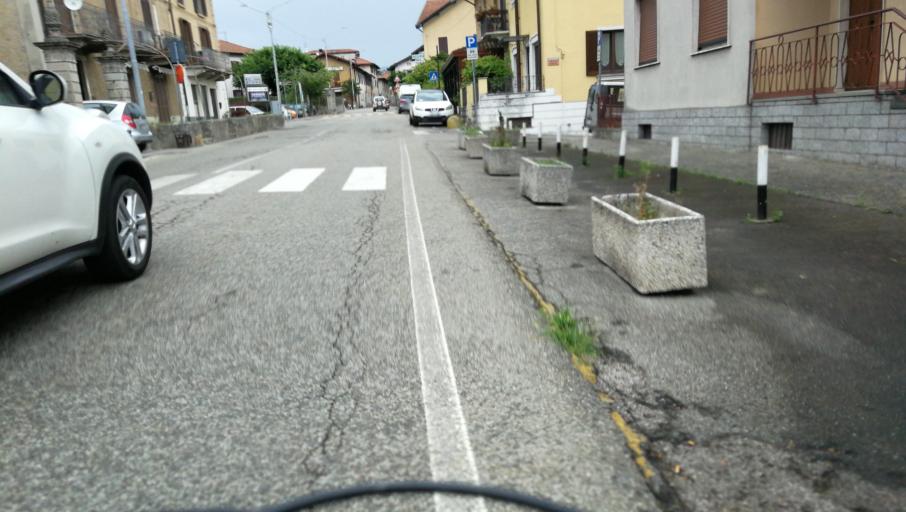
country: IT
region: Lombardy
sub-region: Provincia di Varese
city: Brenta
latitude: 45.8934
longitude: 8.6823
